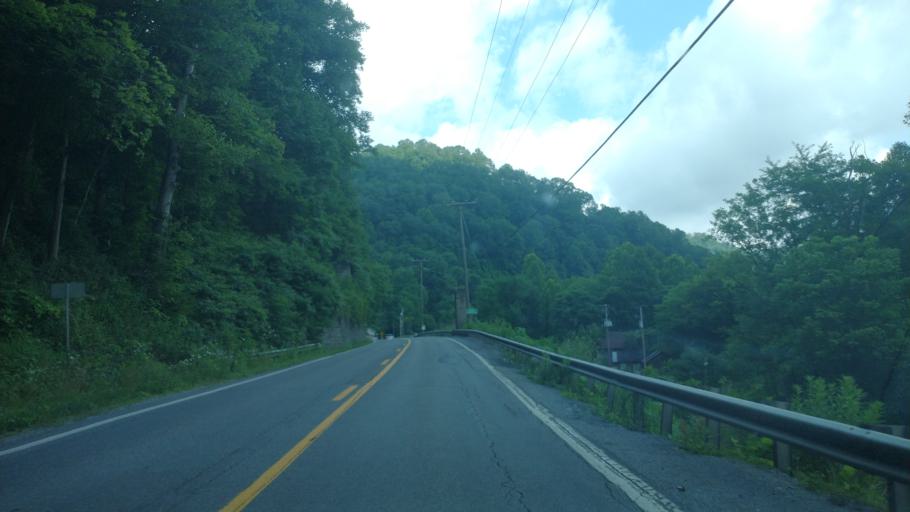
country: US
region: West Virginia
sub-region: McDowell County
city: Welch
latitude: 37.3872
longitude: -81.4195
